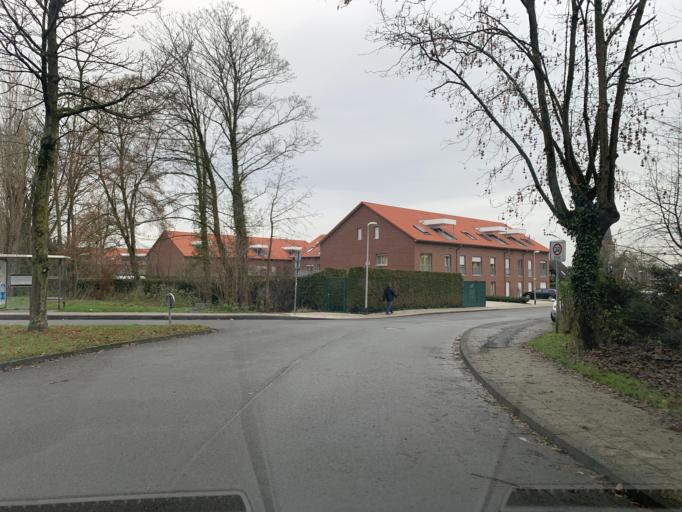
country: DE
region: North Rhine-Westphalia
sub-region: Regierungsbezirk Munster
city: Muenster
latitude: 51.8842
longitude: 7.5997
